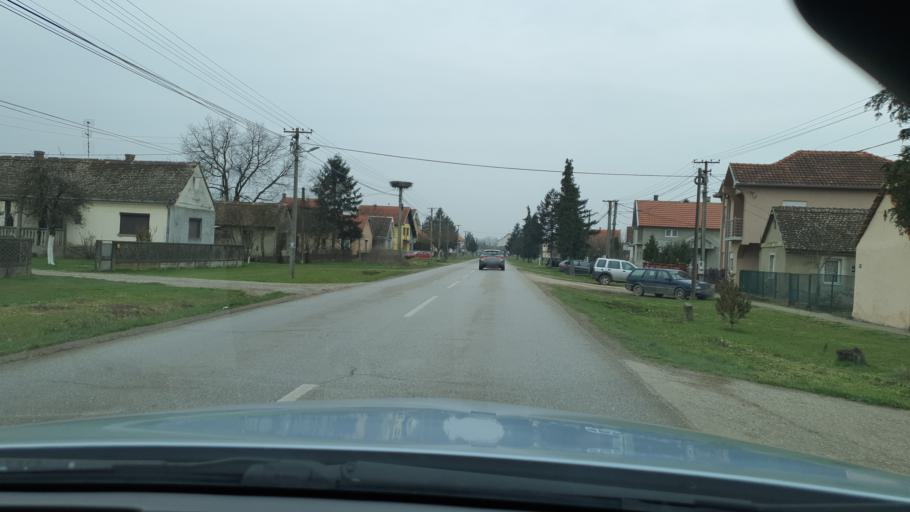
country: RS
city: Belotic
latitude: 44.8160
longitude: 19.5407
